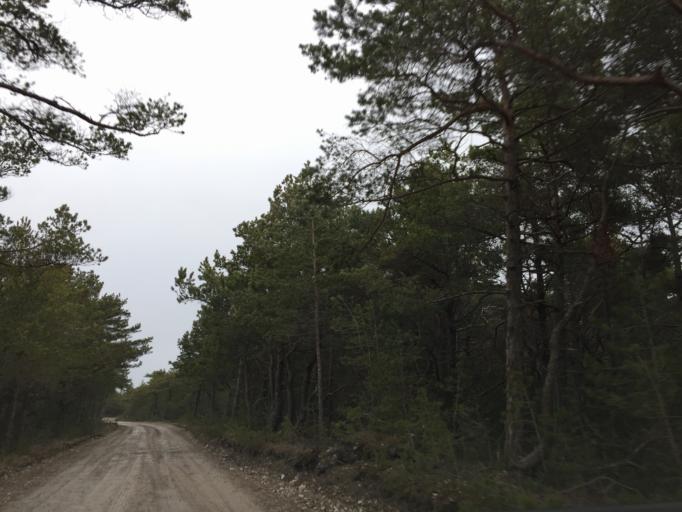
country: EE
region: Saare
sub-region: Kuressaare linn
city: Kuressaare
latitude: 58.5045
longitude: 21.9117
